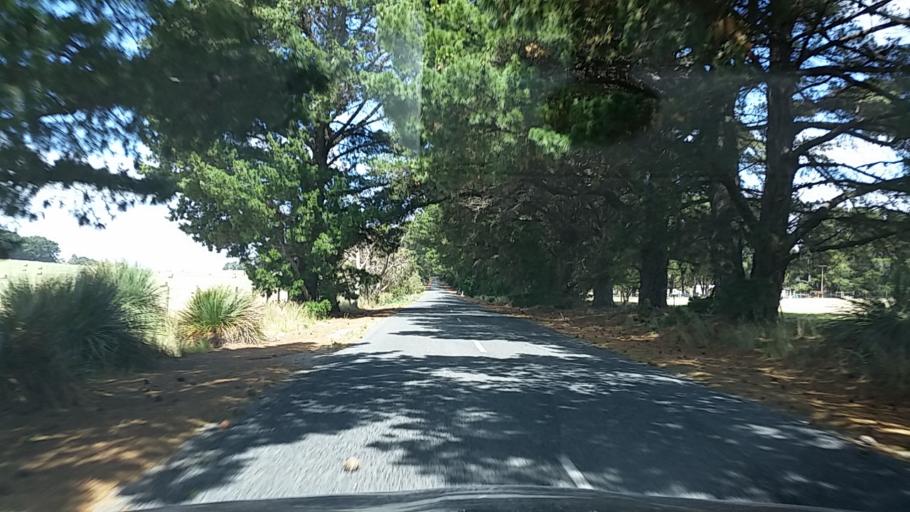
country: AU
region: South Australia
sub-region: Alexandrina
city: Mount Compass
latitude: -35.4398
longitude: 138.6148
